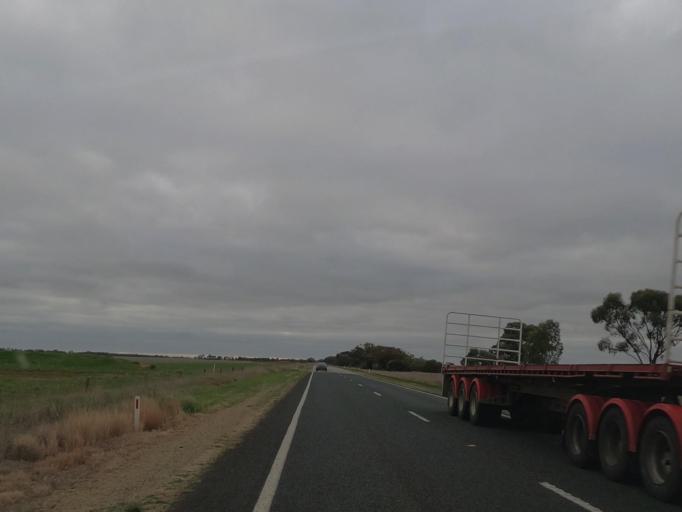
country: AU
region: Victoria
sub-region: Greater Bendigo
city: Long Gully
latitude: -36.2369
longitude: 143.9579
